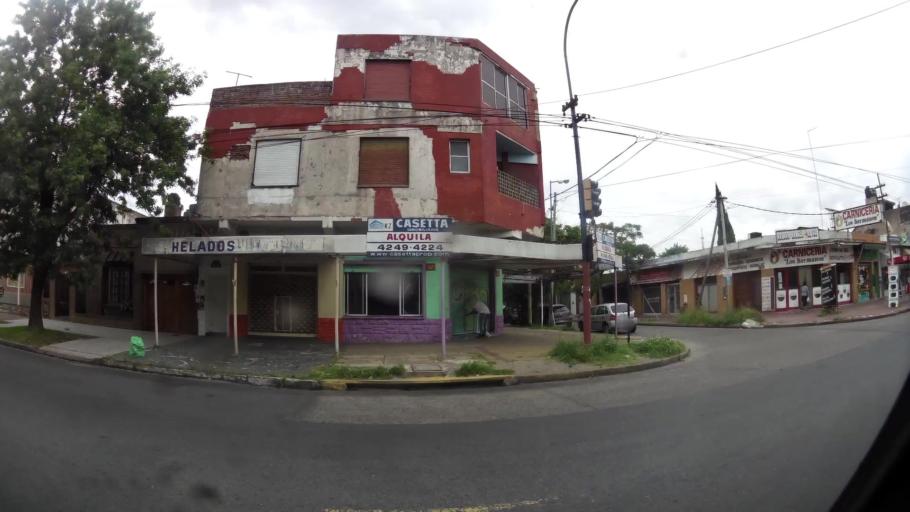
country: AR
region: Buenos Aires
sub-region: Partido de Lanus
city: Lanus
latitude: -34.6937
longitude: -58.3976
